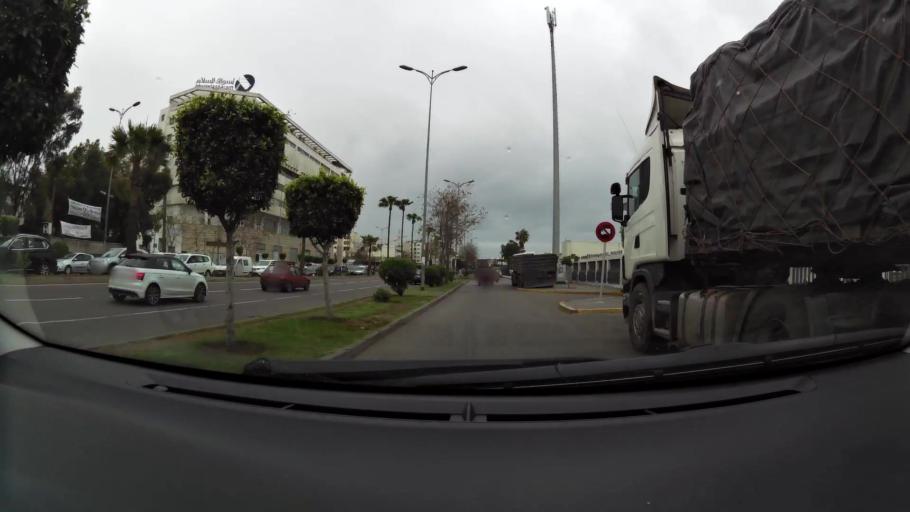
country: MA
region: Grand Casablanca
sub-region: Casablanca
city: Casablanca
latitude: 33.5804
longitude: -7.5916
